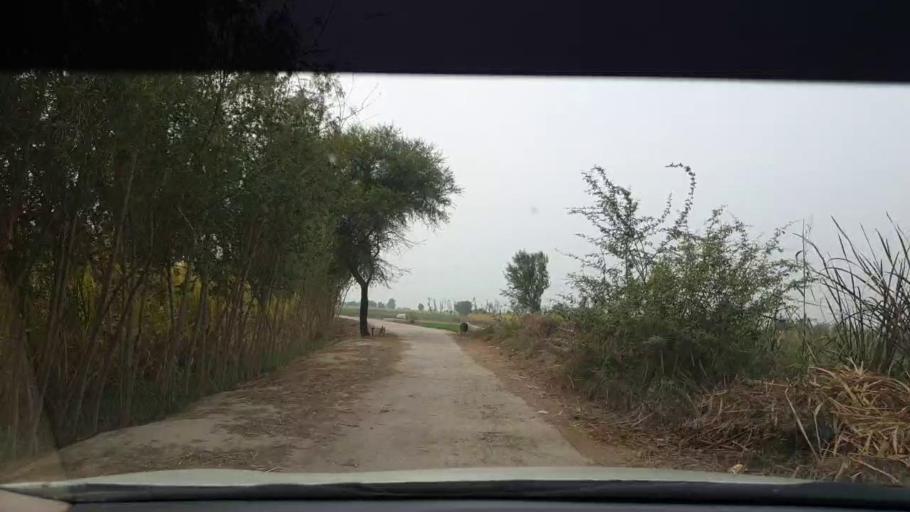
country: PK
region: Sindh
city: Berani
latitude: 25.8648
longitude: 68.7944
